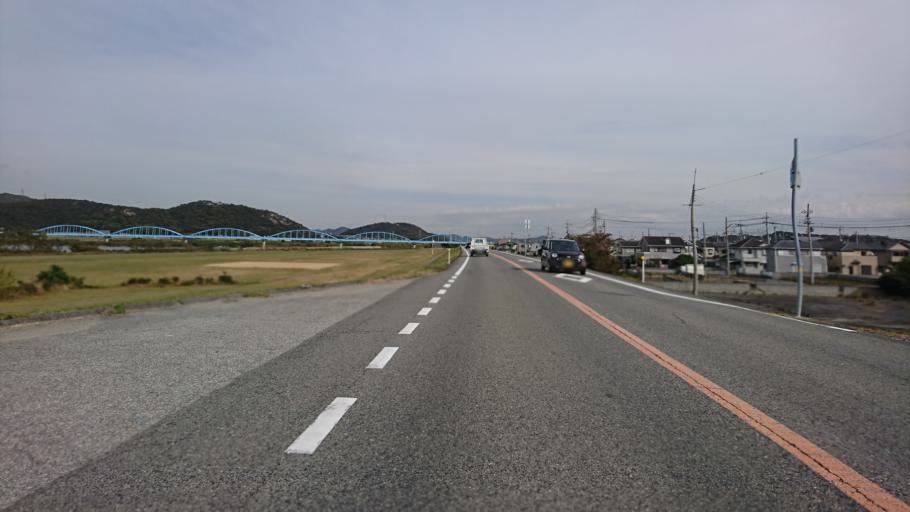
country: JP
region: Hyogo
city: Kakogawacho-honmachi
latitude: 34.7769
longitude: 134.8437
